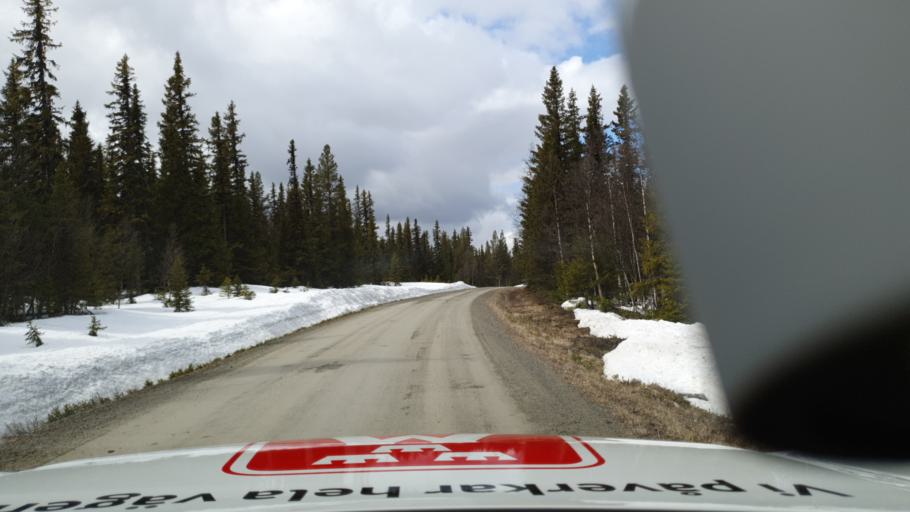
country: SE
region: Jaemtland
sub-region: Bergs Kommun
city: Hoverberg
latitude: 62.8481
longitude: 13.8640
